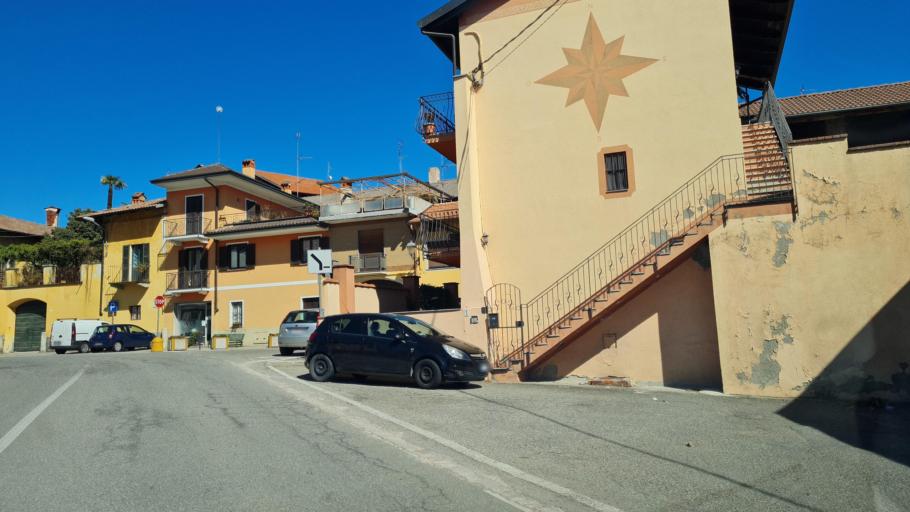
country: IT
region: Piedmont
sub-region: Provincia di Novara
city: Boca
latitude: 45.6789
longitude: 8.4087
